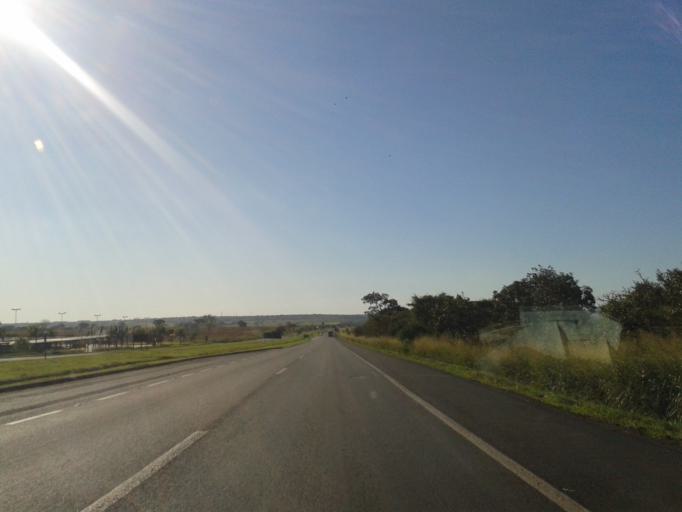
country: BR
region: Minas Gerais
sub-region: Uberlandia
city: Uberlandia
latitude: -19.0156
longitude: -48.2067
